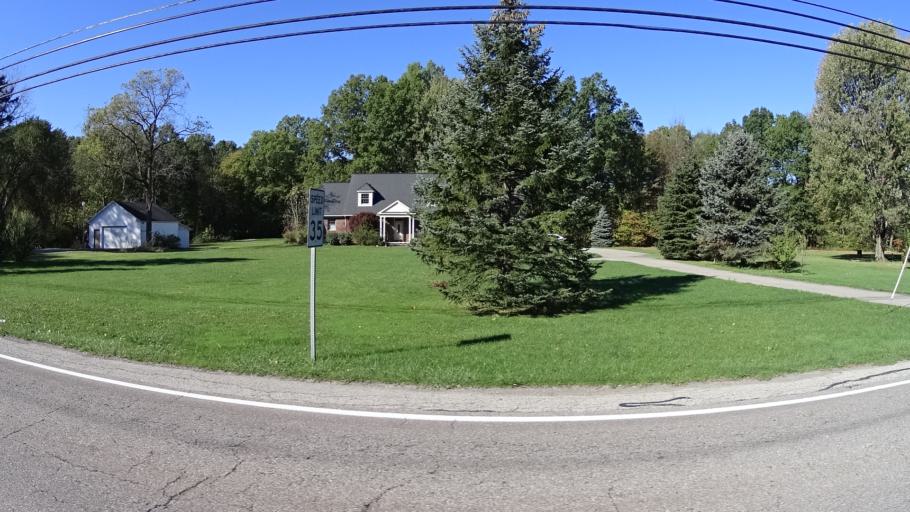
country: US
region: Ohio
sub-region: Lorain County
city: South Amherst
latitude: 41.3678
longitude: -82.2391
